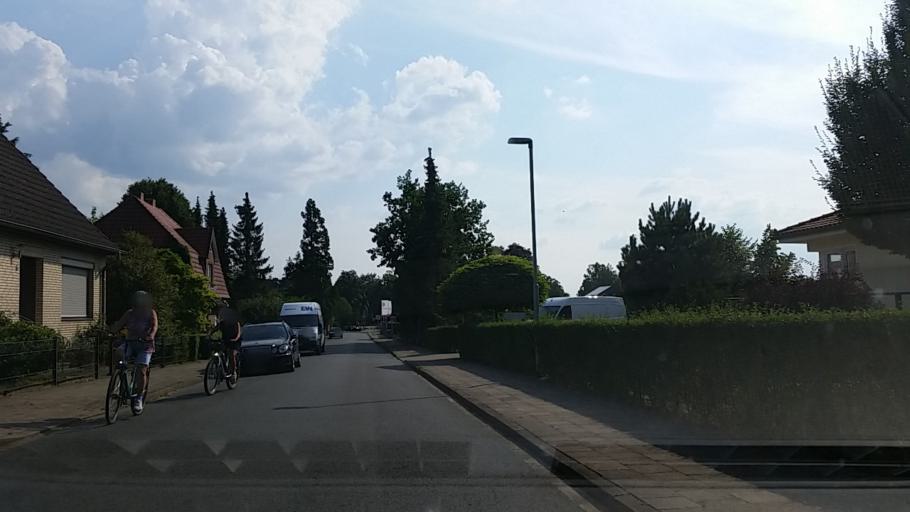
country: DE
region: Lower Saxony
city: Schneverdingen
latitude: 53.1215
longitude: 9.7946
